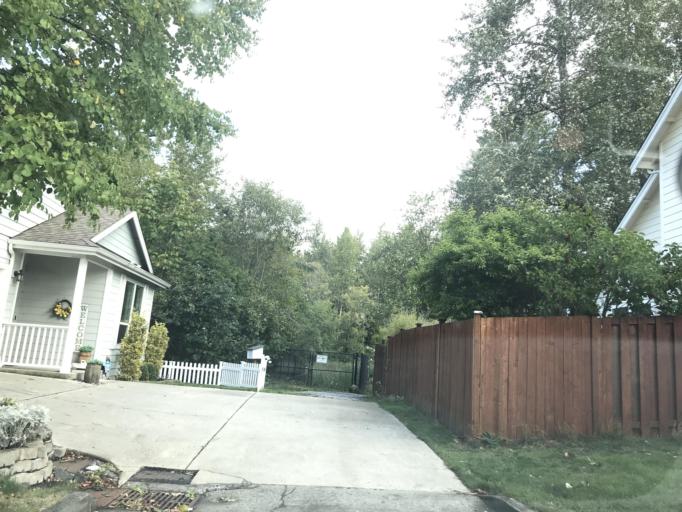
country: US
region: Washington
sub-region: Whatcom County
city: Bellingham
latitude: 48.7924
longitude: -122.5029
